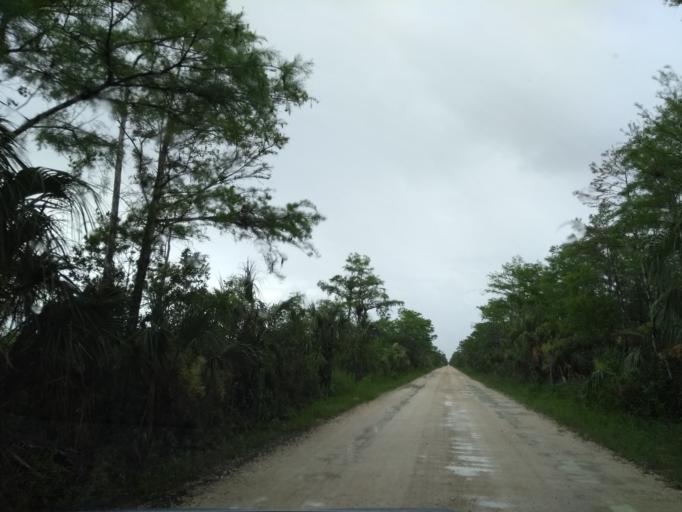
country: US
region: Florida
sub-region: Miami-Dade County
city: The Hammocks
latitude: 25.7602
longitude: -81.0189
